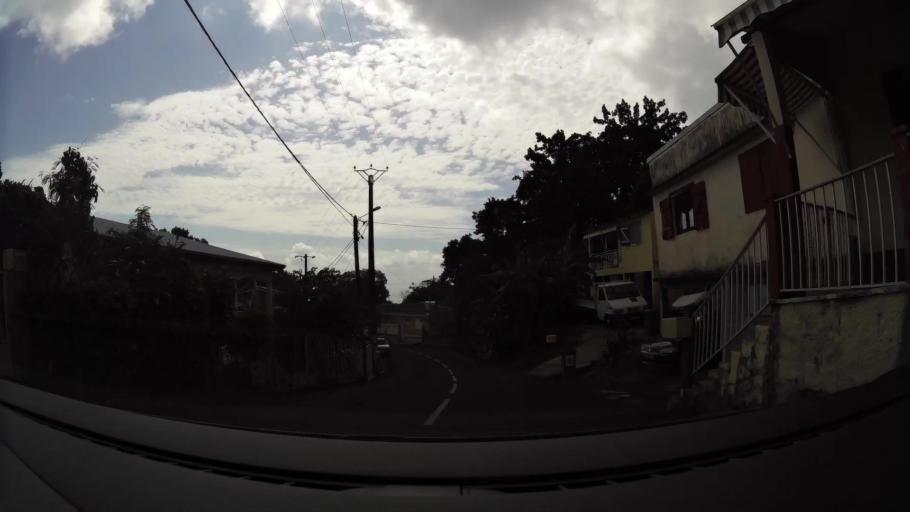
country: GP
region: Guadeloupe
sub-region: Guadeloupe
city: Trois-Rivieres
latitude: 15.9725
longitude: -61.6437
